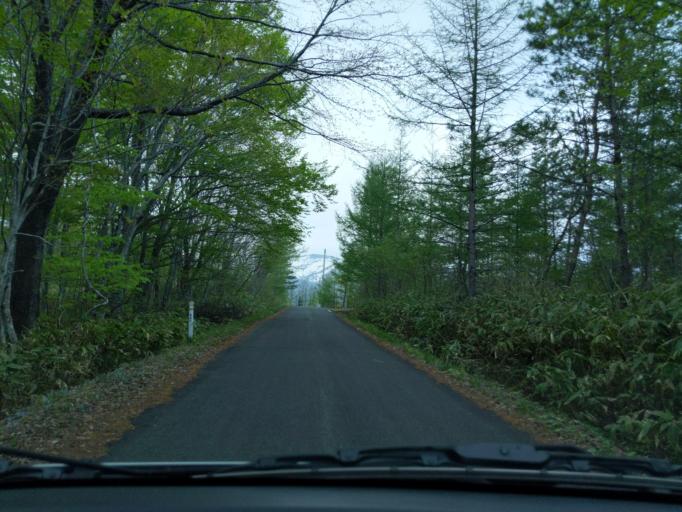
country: JP
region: Iwate
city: Ichinoseki
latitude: 38.9212
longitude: 140.8394
